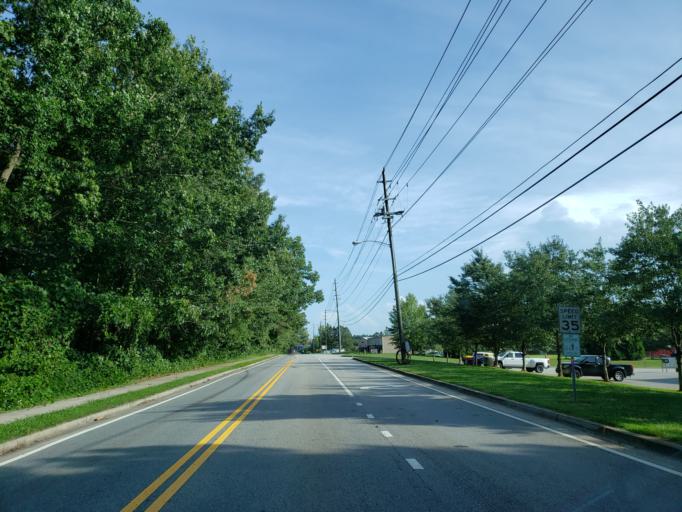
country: US
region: Georgia
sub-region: Cobb County
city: Powder Springs
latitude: 33.8812
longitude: -84.7041
